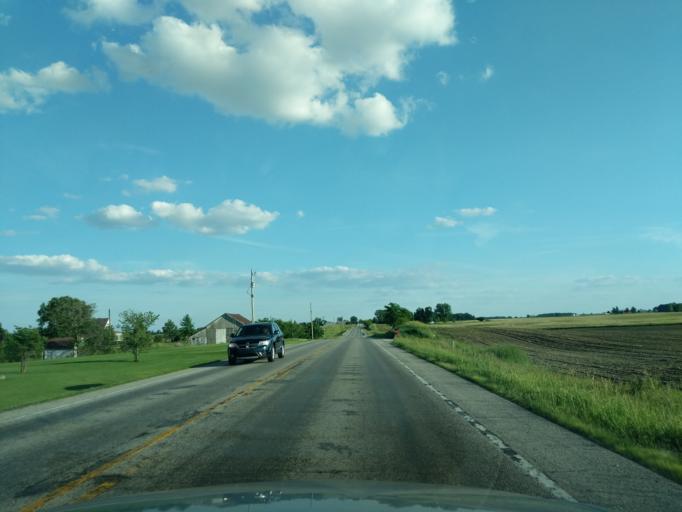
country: US
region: Indiana
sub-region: Huntington County
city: Huntington
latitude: 40.8238
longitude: -85.4654
